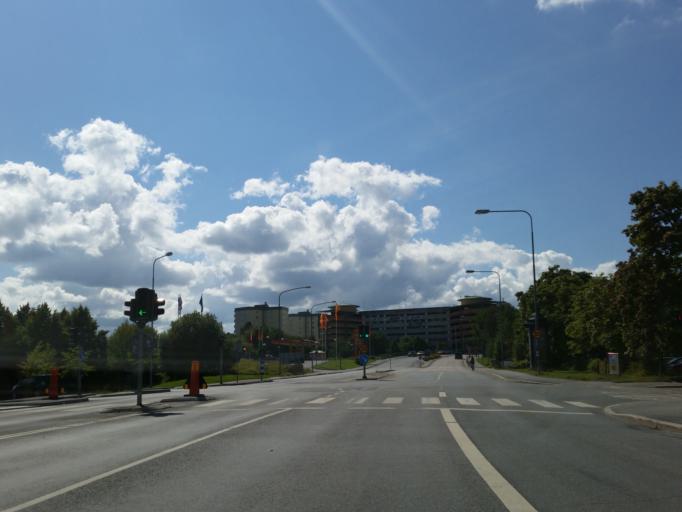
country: SE
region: Stockholm
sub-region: Solna Kommun
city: Solna
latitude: 59.3512
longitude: 18.0047
